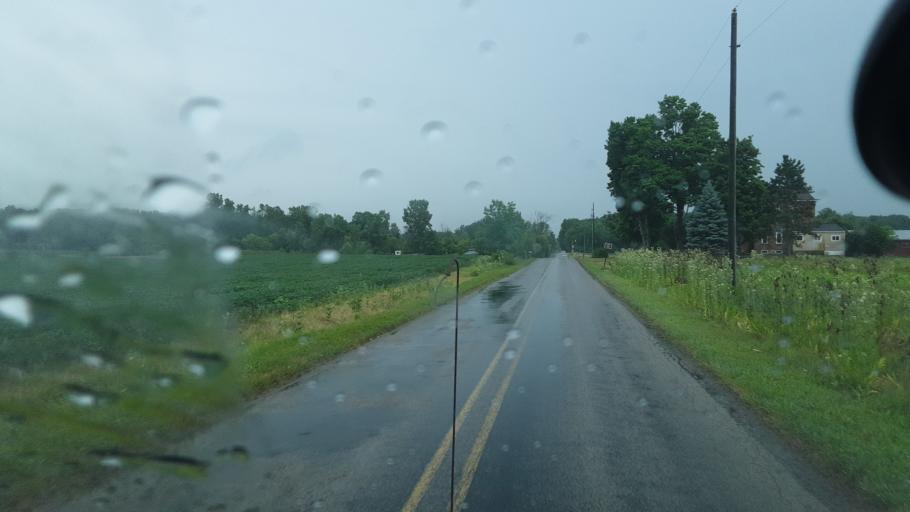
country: US
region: Ohio
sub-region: Williams County
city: Edgerton
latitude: 41.4770
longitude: -84.8144
